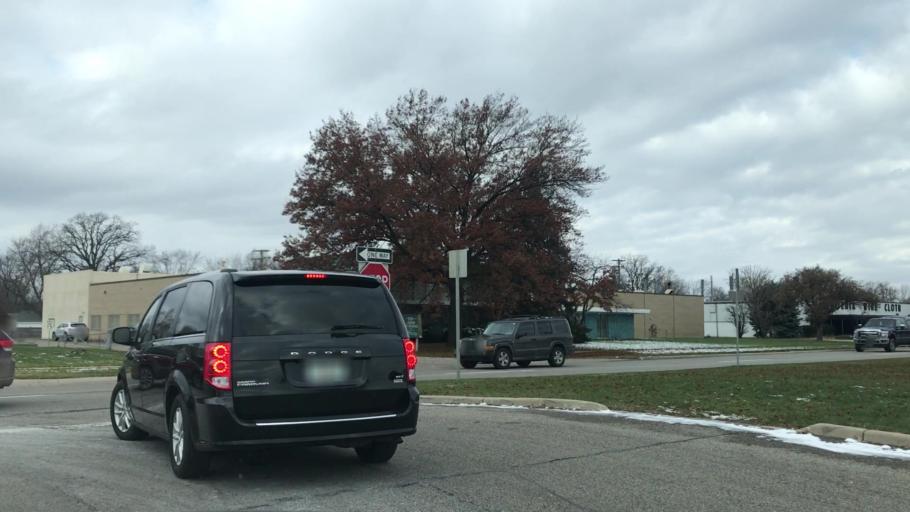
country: US
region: Michigan
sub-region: Oakland County
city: Clawson
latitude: 42.5376
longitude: -83.1202
